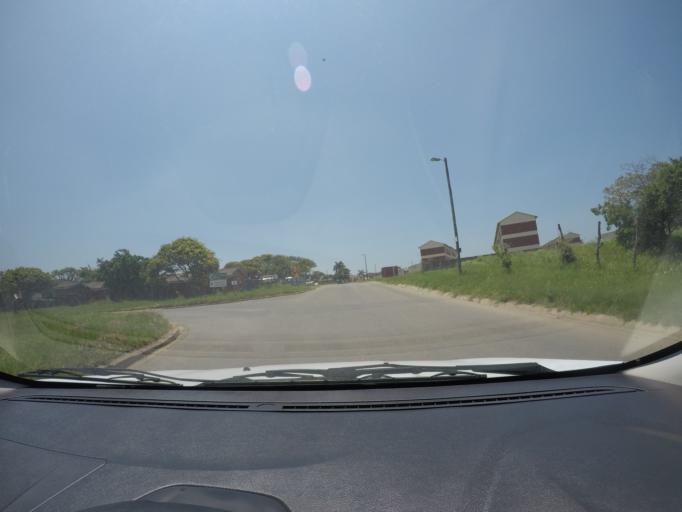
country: ZA
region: KwaZulu-Natal
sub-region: uThungulu District Municipality
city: eSikhawini
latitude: -28.8773
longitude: 31.9027
